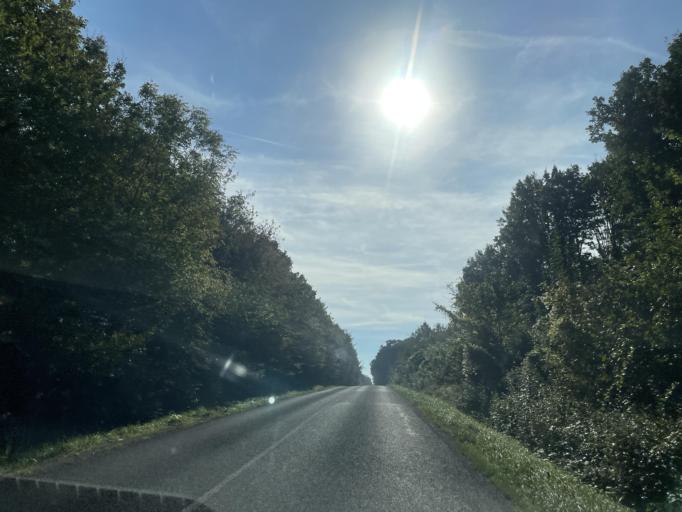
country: FR
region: Ile-de-France
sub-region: Departement de Seine-et-Marne
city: Saint-Jean-les-Deux-Jumeaux
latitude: 48.9549
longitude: 2.9864
